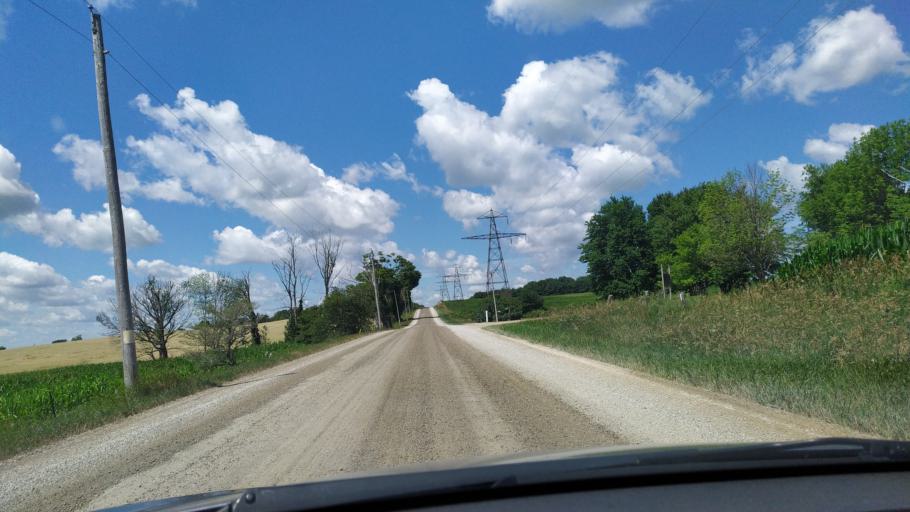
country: CA
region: Ontario
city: Stratford
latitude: 43.3879
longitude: -80.8292
